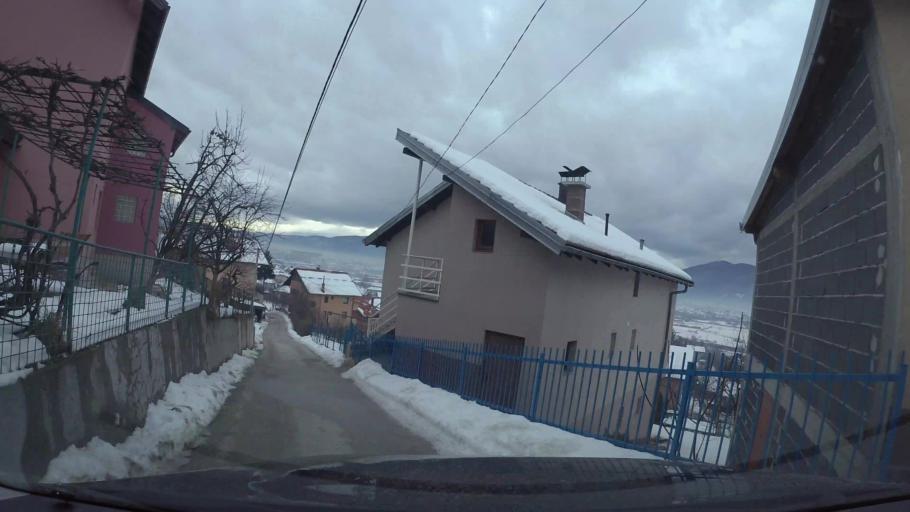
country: BA
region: Federation of Bosnia and Herzegovina
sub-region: Kanton Sarajevo
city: Sarajevo
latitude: 43.8654
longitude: 18.3206
